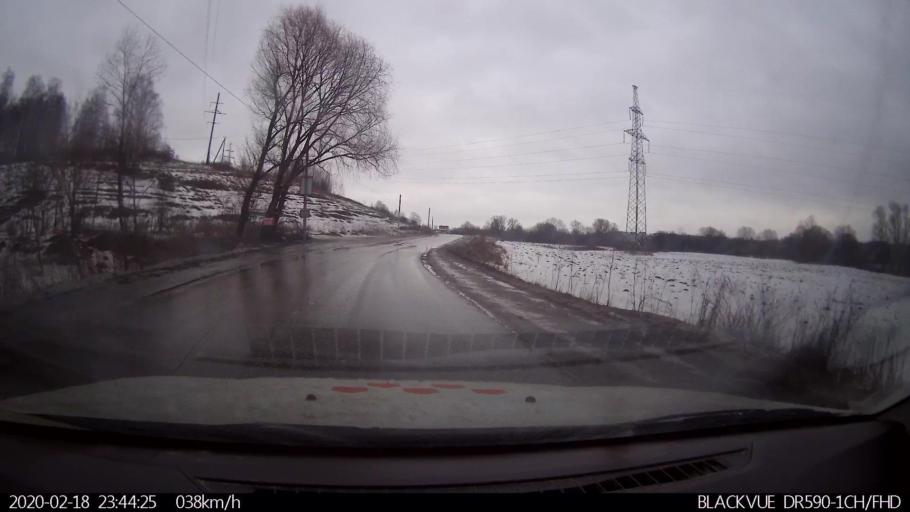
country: RU
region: Nizjnij Novgorod
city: Afonino
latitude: 56.2428
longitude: 44.0894
